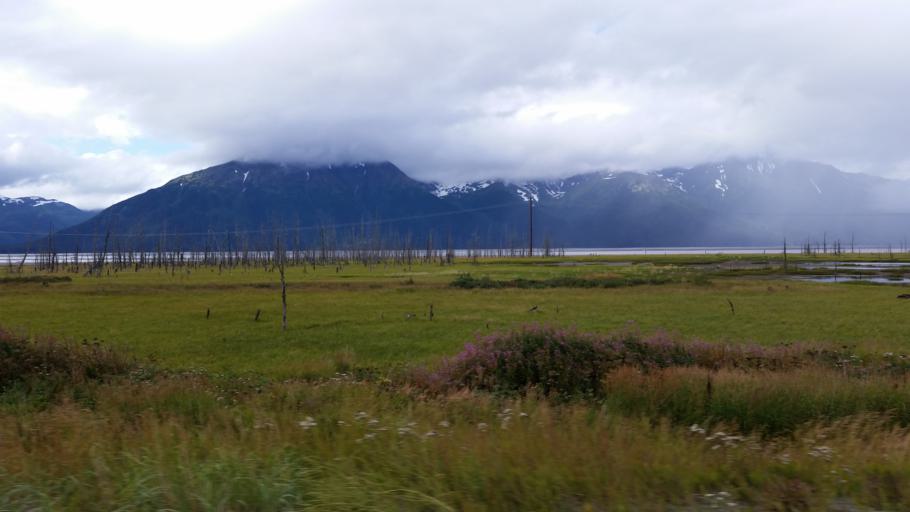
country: US
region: Alaska
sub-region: Anchorage Municipality
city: Girdwood
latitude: 60.9407
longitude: -149.1750
